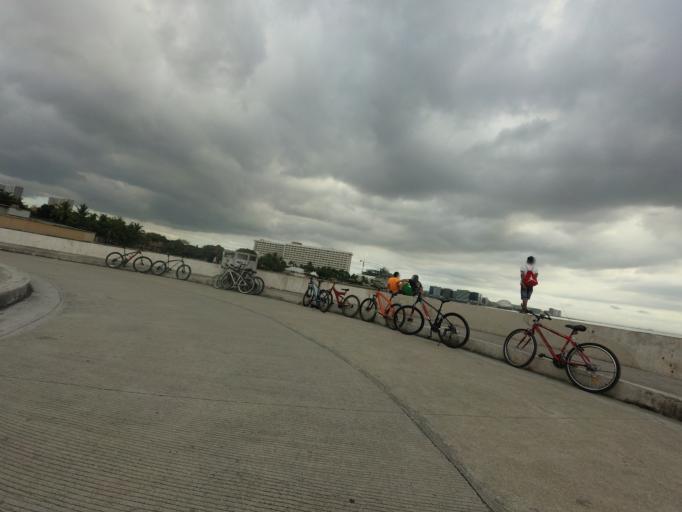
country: PH
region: Metro Manila
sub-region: City of Manila
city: Port Area
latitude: 14.5555
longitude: 120.9777
